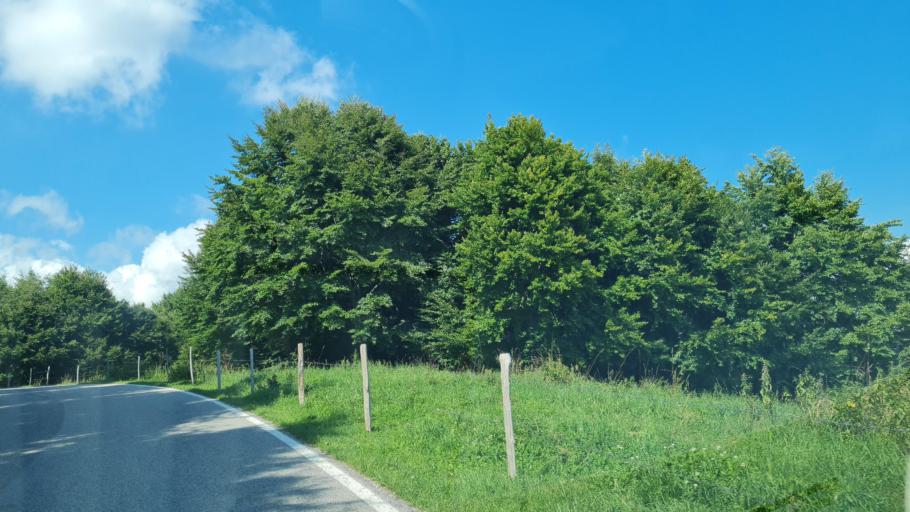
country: IT
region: Veneto
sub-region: Provincia di Vicenza
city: Conco
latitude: 45.8073
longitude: 11.6462
